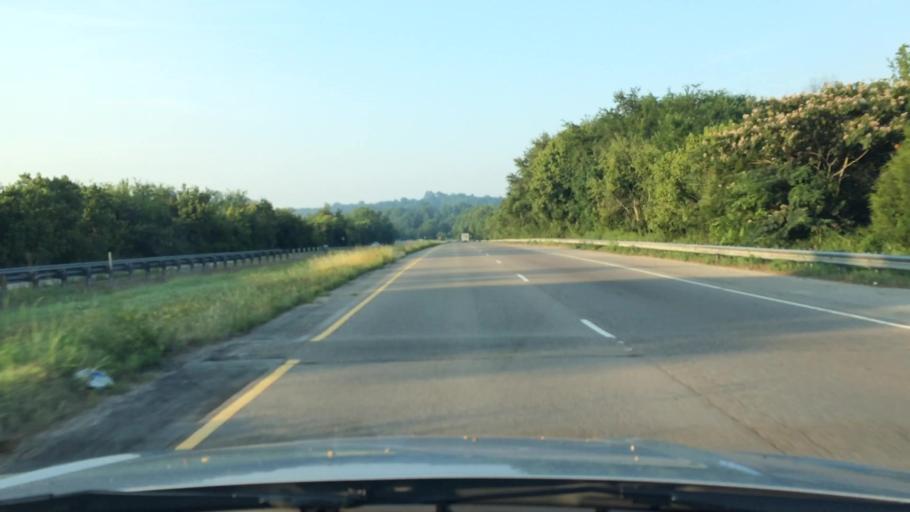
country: US
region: Tennessee
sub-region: Giles County
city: Pulaski
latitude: 35.1941
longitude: -87.0643
